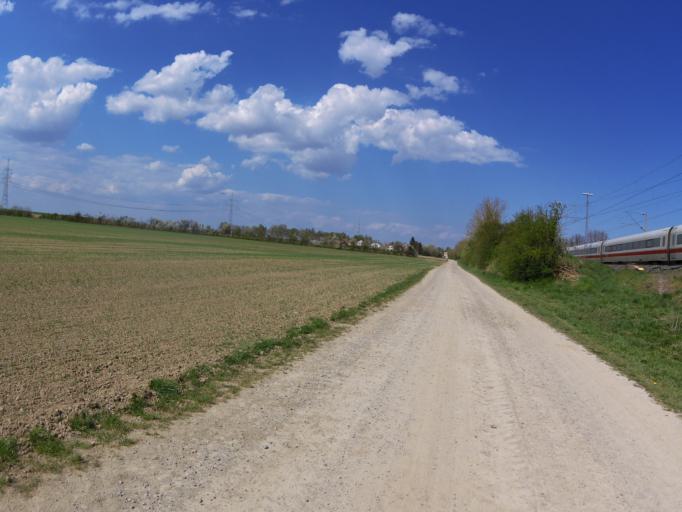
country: DE
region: Bavaria
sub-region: Regierungsbezirk Unterfranken
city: Oberpleichfeld
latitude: 49.8479
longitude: 10.1029
